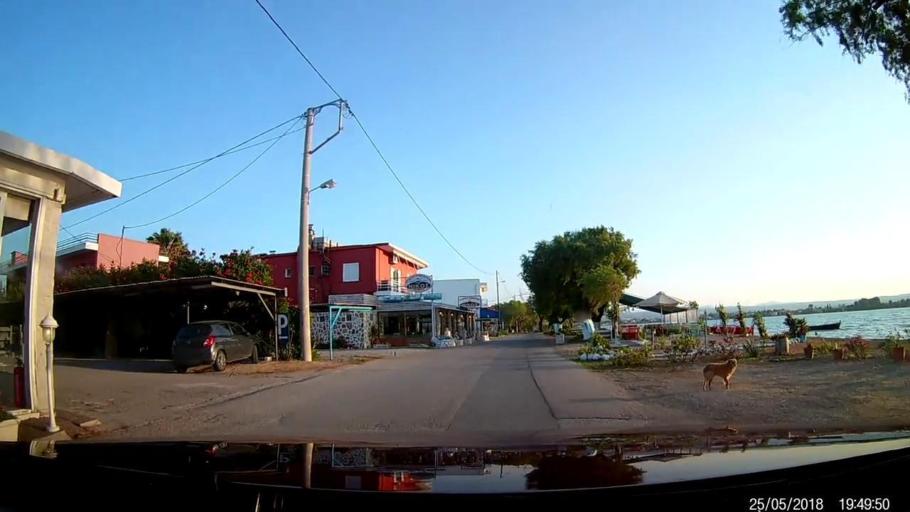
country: GR
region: Central Greece
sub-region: Nomos Evvoias
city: Ayios Nikolaos
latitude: 38.4092
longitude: 23.6404
